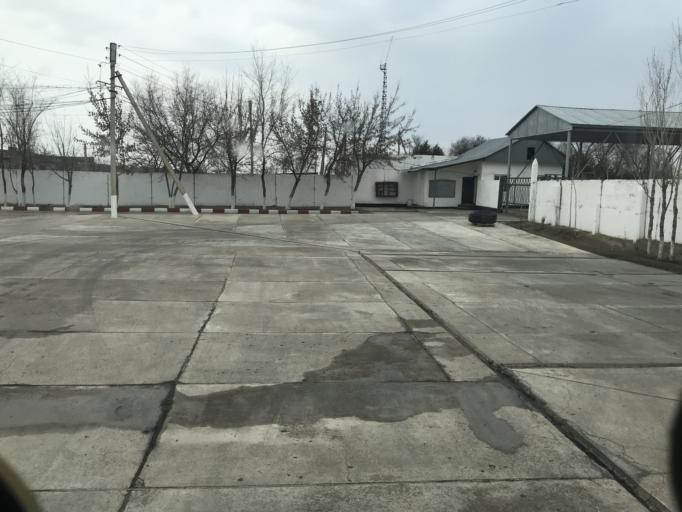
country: KZ
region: Ongtustik Qazaqstan
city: Shardara
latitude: 41.2491
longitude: 67.9015
